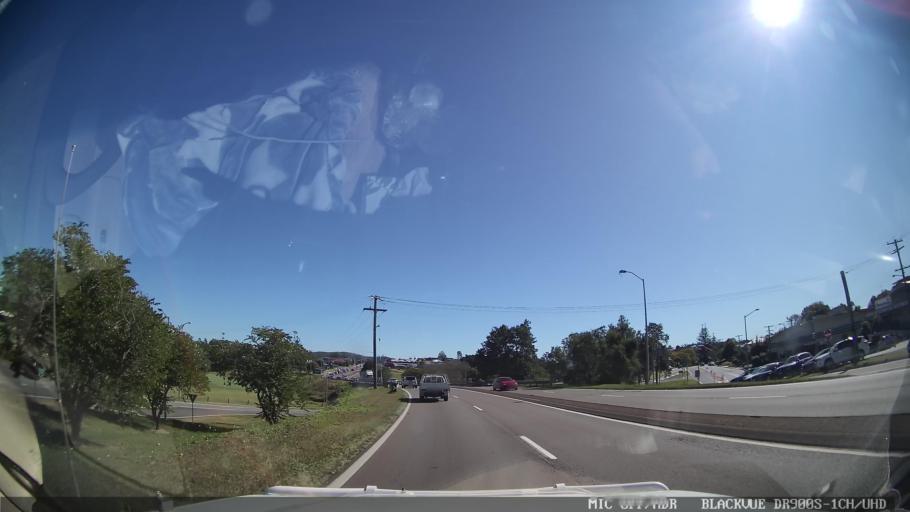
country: AU
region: Queensland
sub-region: Gympie Regional Council
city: Gympie
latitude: -26.1943
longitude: 152.6611
